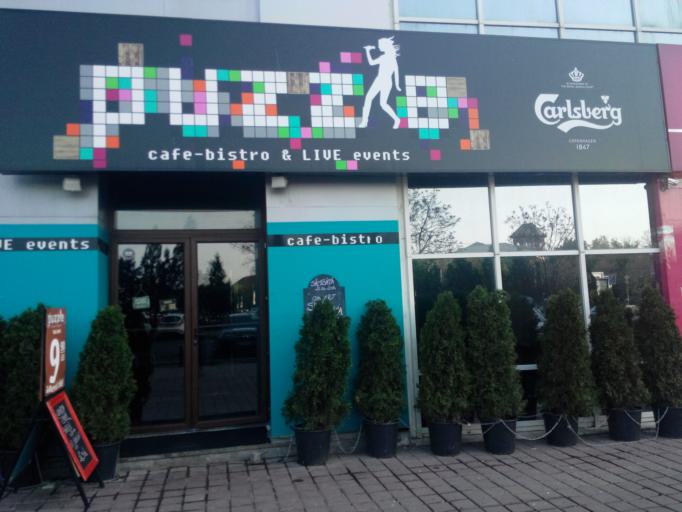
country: RO
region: Bucuresti
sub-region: Municipiul Bucuresti
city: Bucuresti
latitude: 44.4516
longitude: 26.0851
